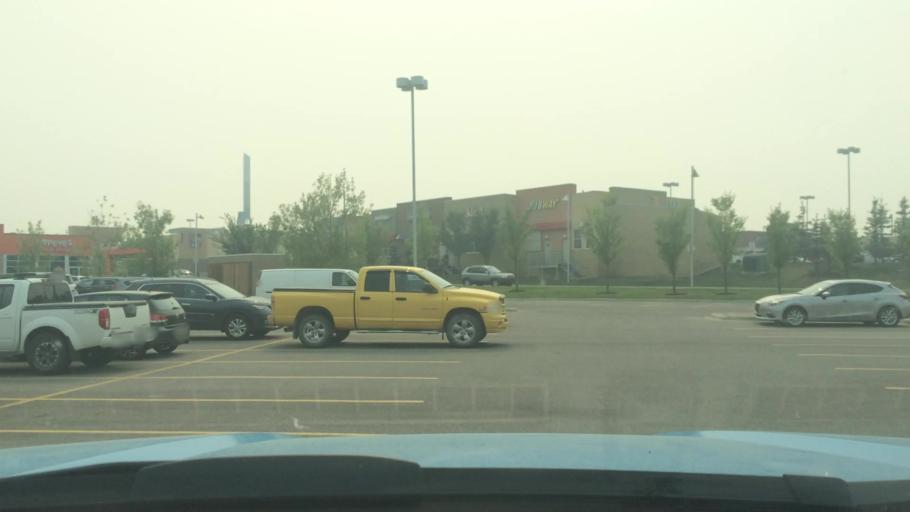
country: CA
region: Alberta
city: Calgary
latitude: 51.1570
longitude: -114.1572
